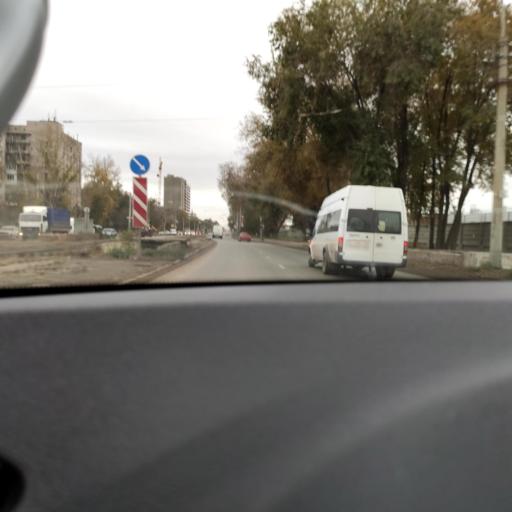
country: RU
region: Samara
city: Smyshlyayevka
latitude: 53.2054
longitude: 50.2793
